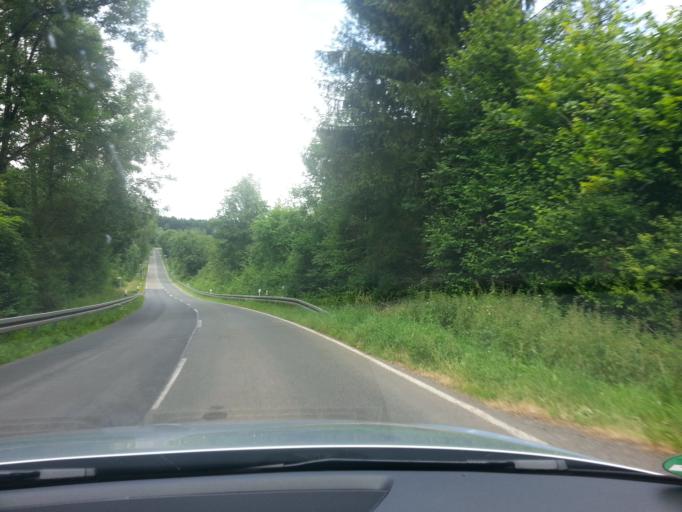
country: DE
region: Saarland
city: Orscholz
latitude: 49.4804
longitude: 6.4950
